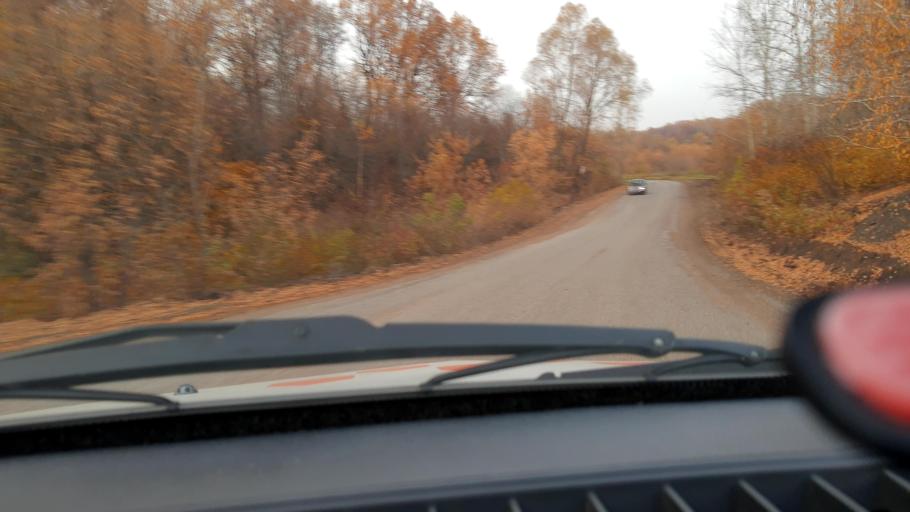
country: RU
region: Bashkortostan
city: Iglino
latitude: 54.7966
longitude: 56.3133
